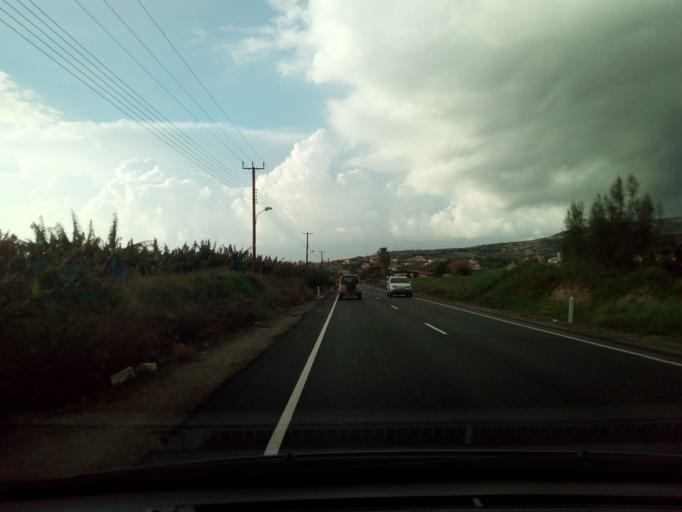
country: CY
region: Pafos
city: Pegeia
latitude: 34.8641
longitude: 32.3698
